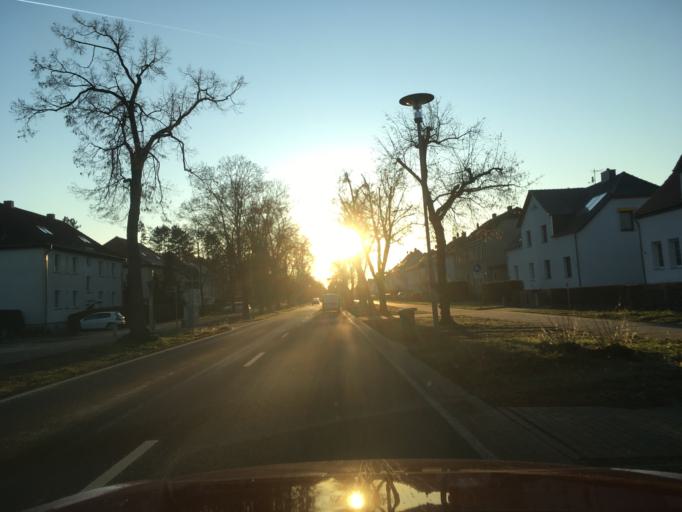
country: DE
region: Saxony-Anhalt
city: Rosslau
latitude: 51.8931
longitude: 12.2642
